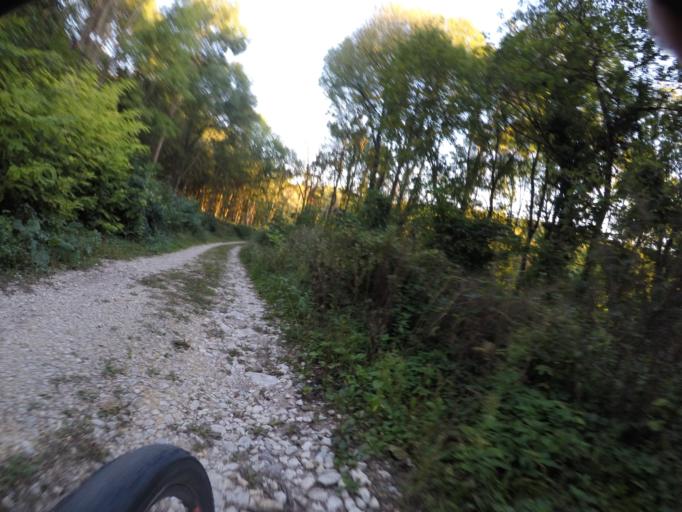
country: AT
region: Lower Austria
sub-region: Politischer Bezirk Bruck an der Leitha
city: Mannersdorf am Leithagebirge
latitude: 47.9565
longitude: 16.5956
